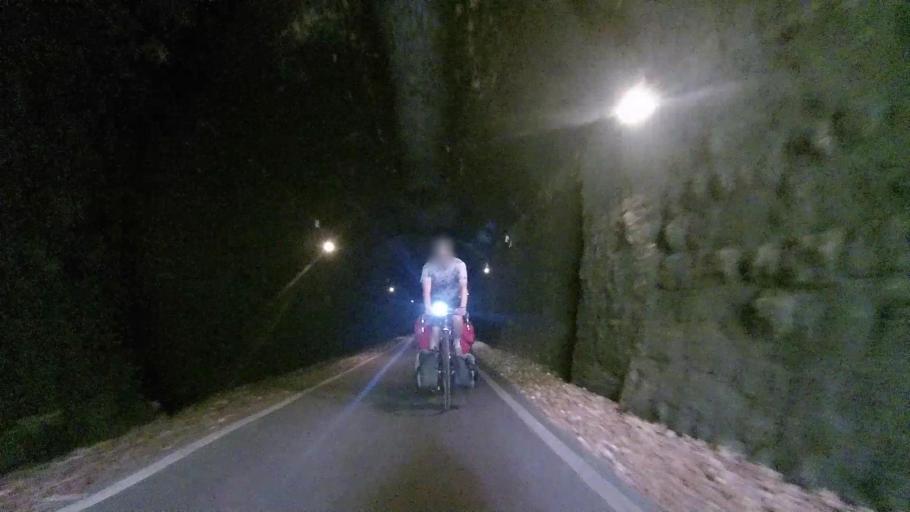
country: GB
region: England
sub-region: Bath and North East Somerset
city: Bath
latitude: 51.3667
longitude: -2.3533
